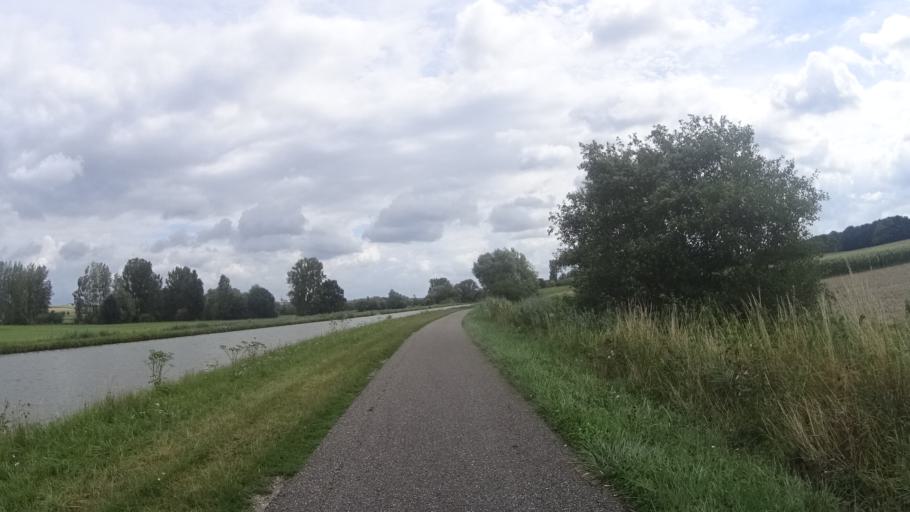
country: FR
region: Alsace
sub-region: Departement du Bas-Rhin
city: Hochfelden
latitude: 48.7432
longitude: 7.5431
